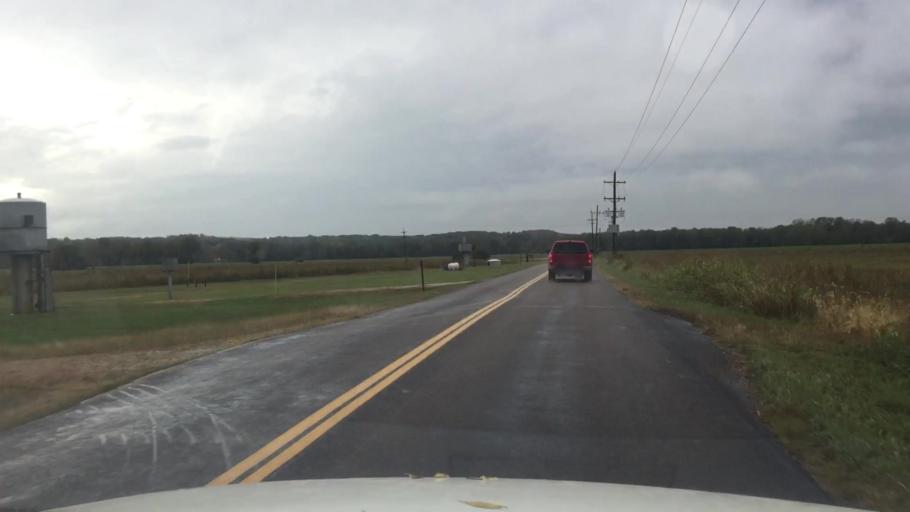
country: US
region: Missouri
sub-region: Boone County
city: Columbia
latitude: 38.8858
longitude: -92.4574
